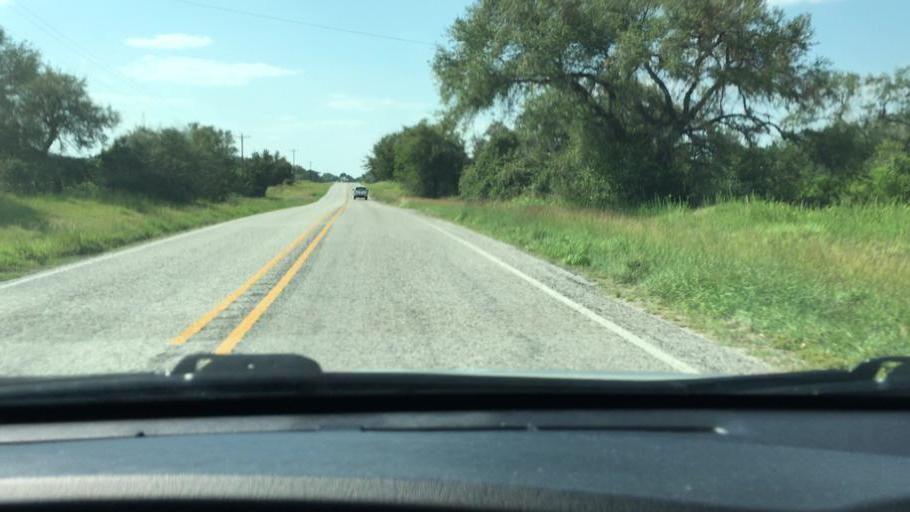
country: US
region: Texas
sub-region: DeWitt County
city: Cuero
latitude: 28.9131
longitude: -97.3221
